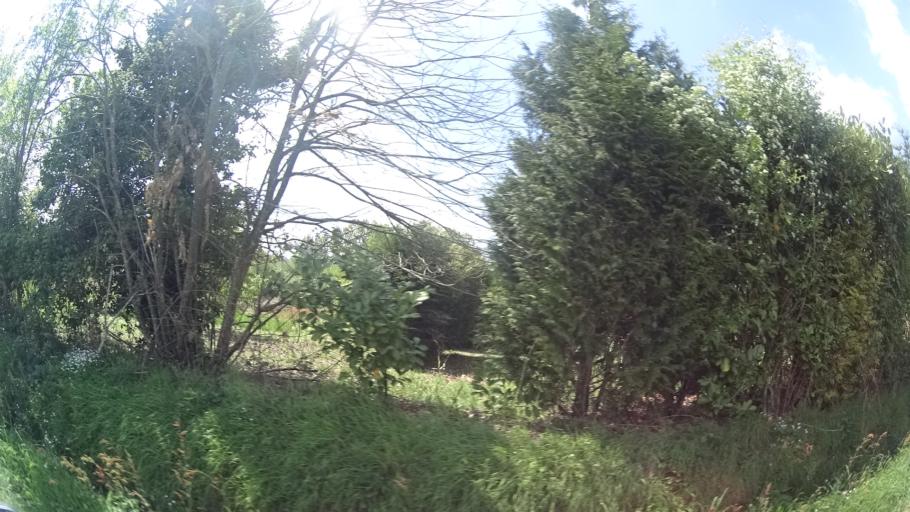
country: FR
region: Brittany
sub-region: Departement du Morbihan
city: Beganne
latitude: 47.5924
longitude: -2.2390
